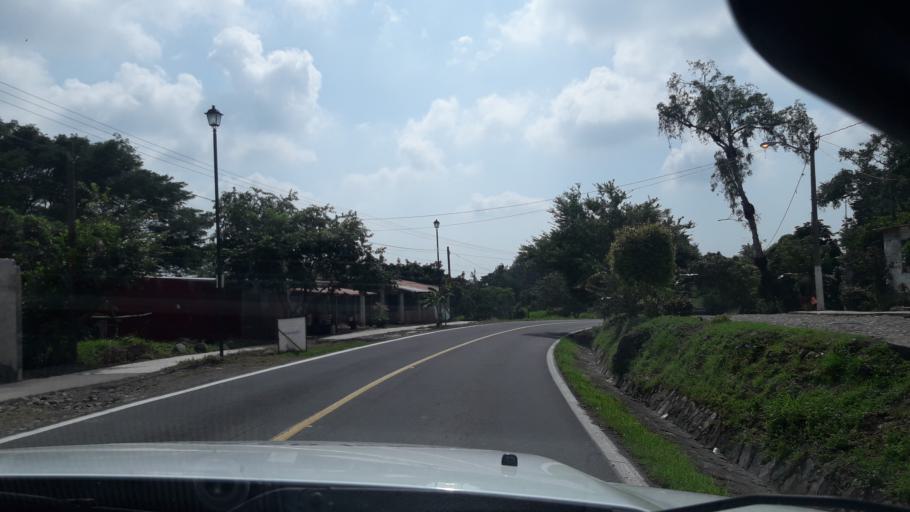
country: MX
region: Colima
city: Suchitlan
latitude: 19.3916
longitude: -103.7060
